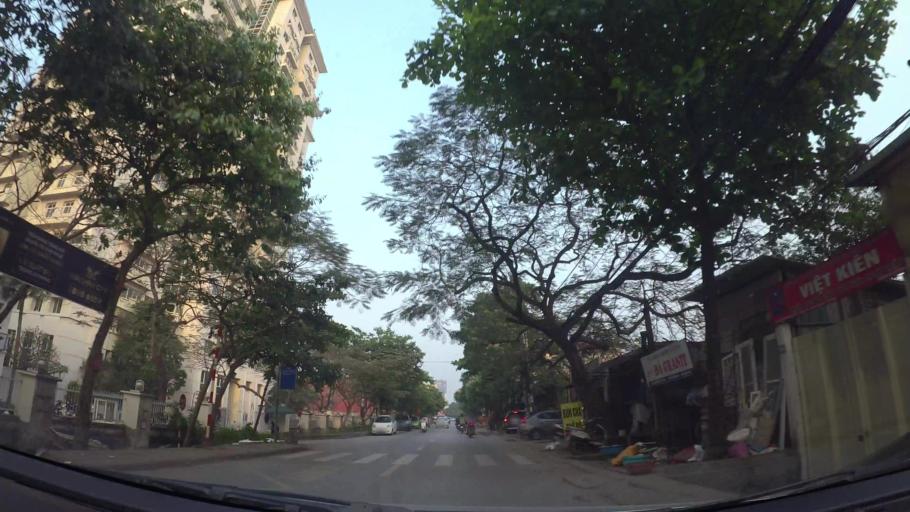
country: VN
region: Ha Noi
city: Tay Ho
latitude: 21.0735
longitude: 105.8008
